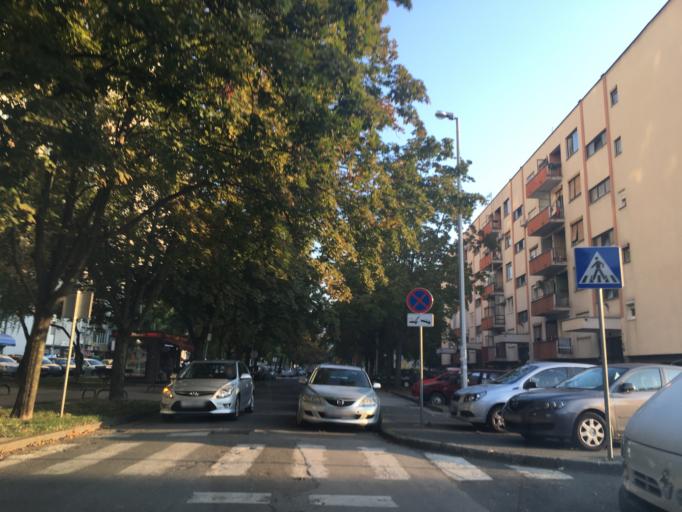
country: HR
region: Grad Zagreb
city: Jankomir
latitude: 45.7893
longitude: 15.9385
